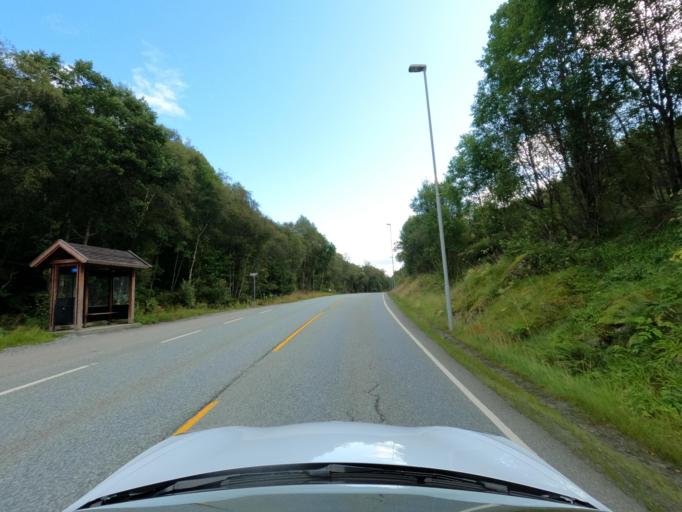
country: NO
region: Hordaland
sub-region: Meland
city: Frekhaug
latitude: 60.4854
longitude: 5.2892
